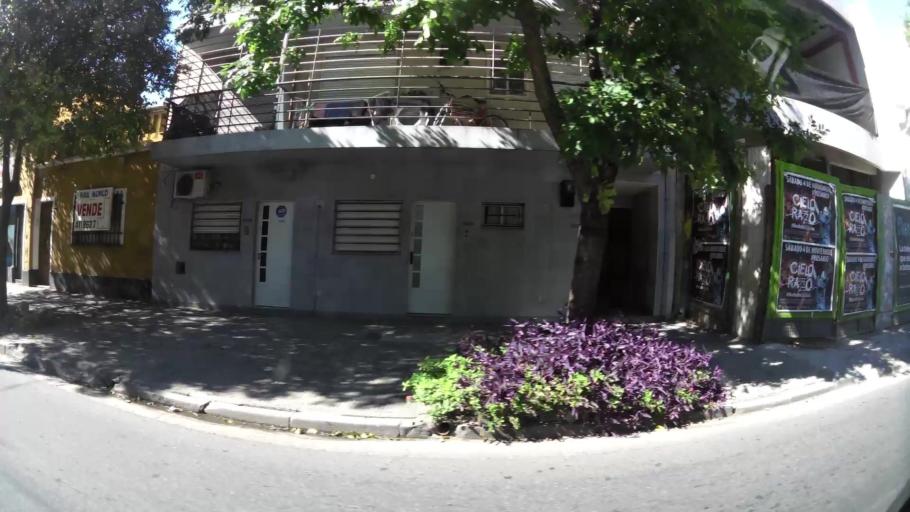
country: AR
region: Santa Fe
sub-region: Departamento de Rosario
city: Rosario
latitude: -32.9442
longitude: -60.6728
